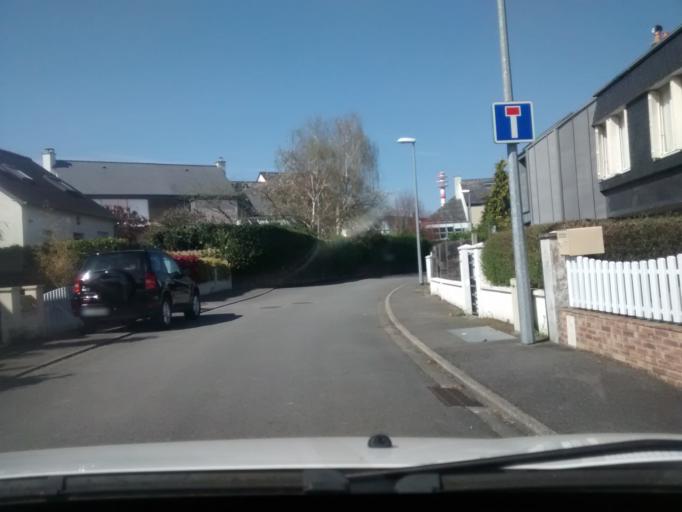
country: FR
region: Brittany
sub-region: Departement d'Ille-et-Vilaine
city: Cesson-Sevigne
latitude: 48.1158
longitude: -1.6280
